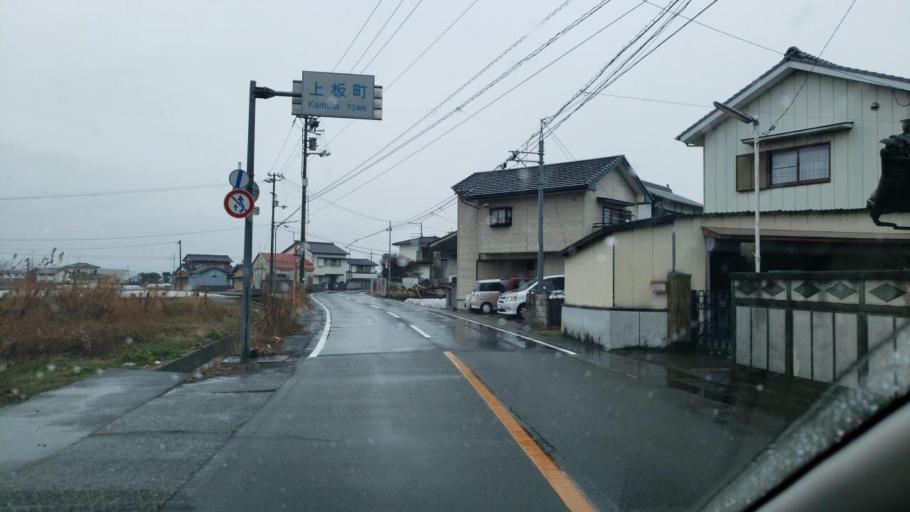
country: JP
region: Tokushima
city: Kamojimacho-jogejima
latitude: 34.0994
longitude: 134.3945
